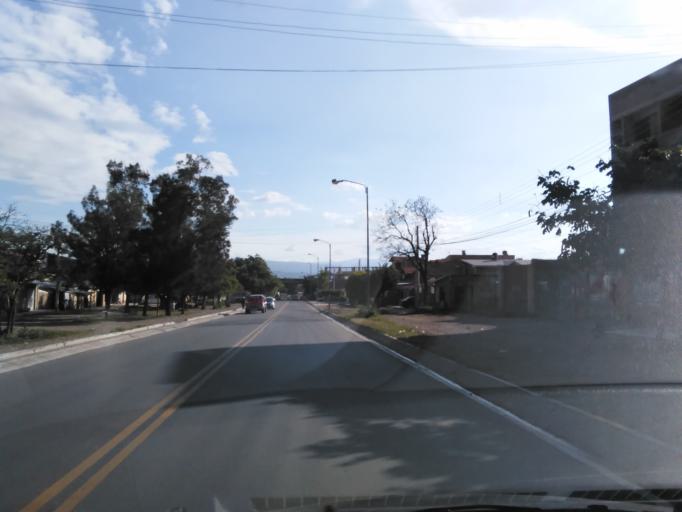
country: BO
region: Cochabamba
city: Cochabamba
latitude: -17.3522
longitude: -66.1862
